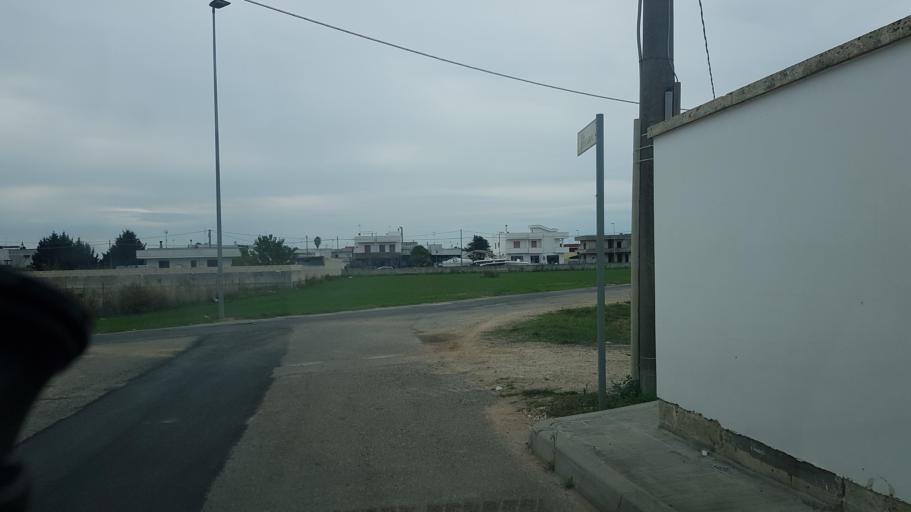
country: IT
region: Apulia
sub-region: Provincia di Lecce
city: Leverano
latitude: 40.2991
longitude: 17.9995
